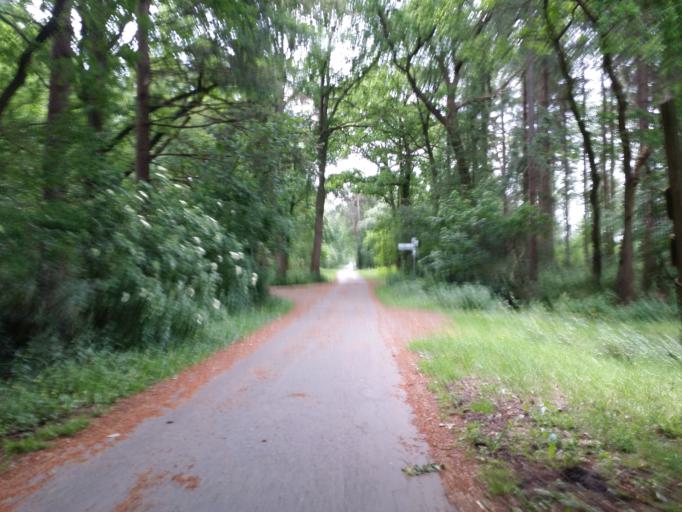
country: DE
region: Lower Saxony
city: Friedeburg
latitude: 53.4919
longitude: 7.8180
